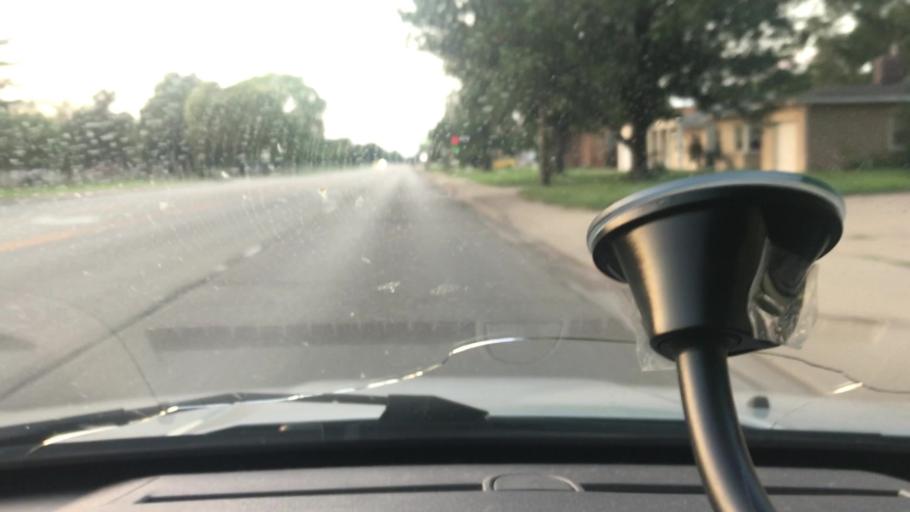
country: US
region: Illinois
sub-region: Tazewell County
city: Pekin
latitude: 40.5848
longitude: -89.6410
